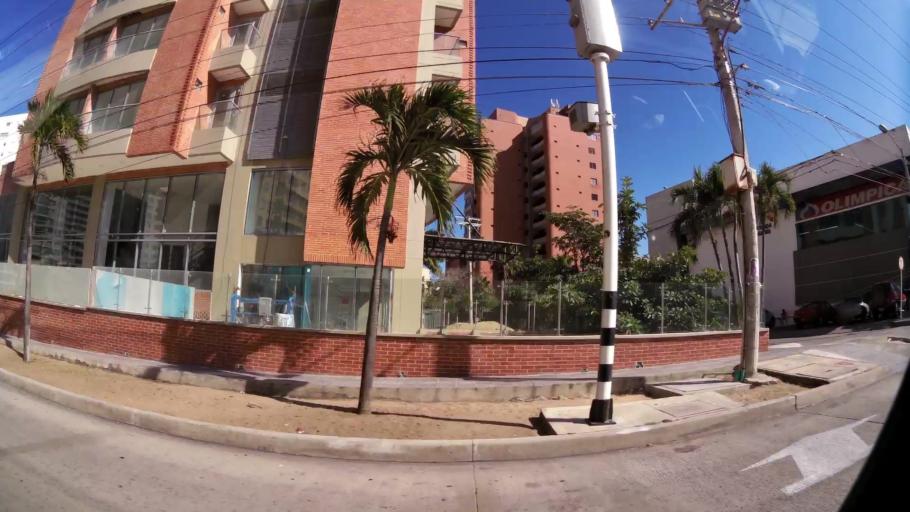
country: CO
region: Atlantico
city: Barranquilla
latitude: 11.0158
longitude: -74.8252
